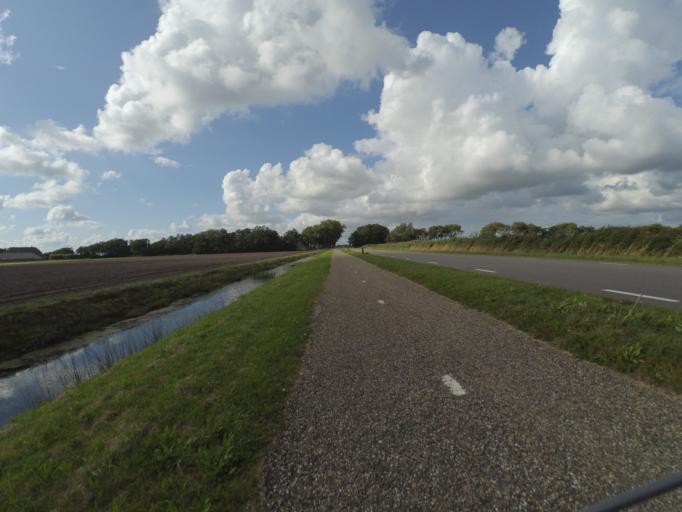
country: NL
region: North Holland
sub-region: Gemeente Schagen
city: Schagen
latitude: 52.8208
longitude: 4.7796
